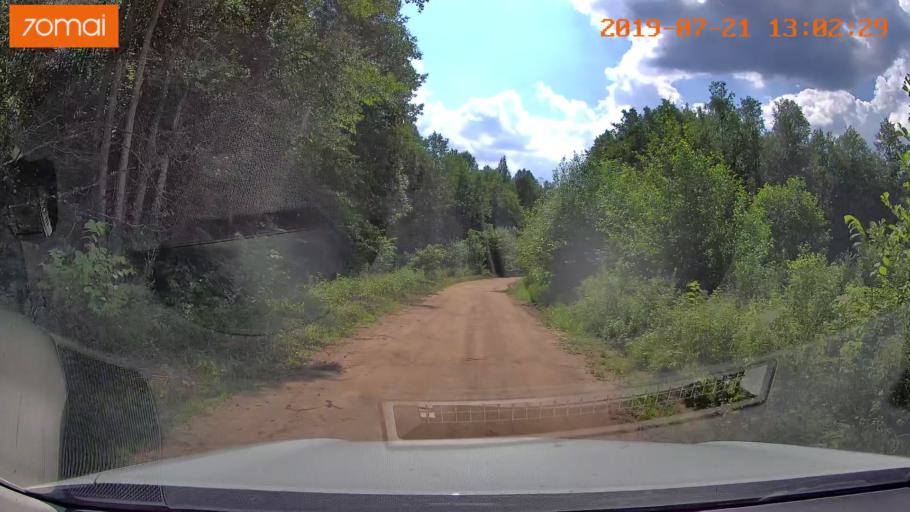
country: BY
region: Grodnenskaya
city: Lyubcha
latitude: 53.8473
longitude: 26.0248
